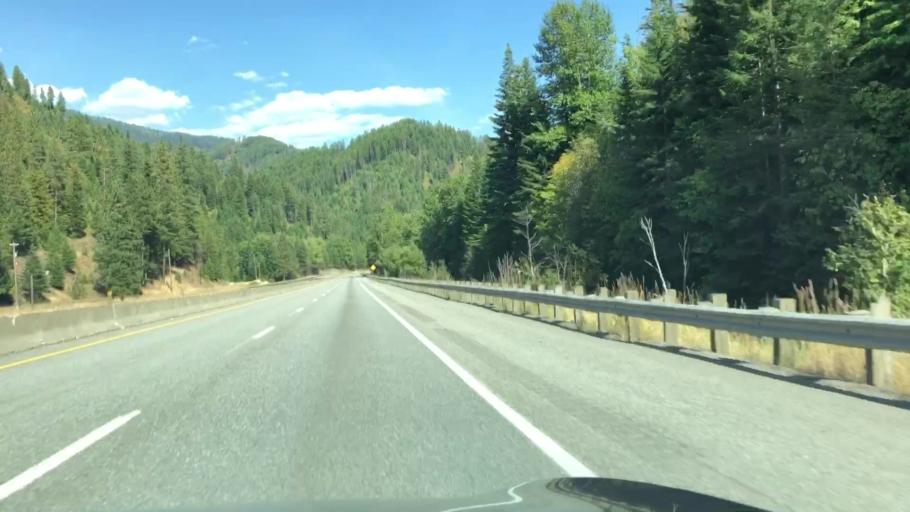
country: US
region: Idaho
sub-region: Shoshone County
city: Wallace
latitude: 47.4740
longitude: -115.8981
